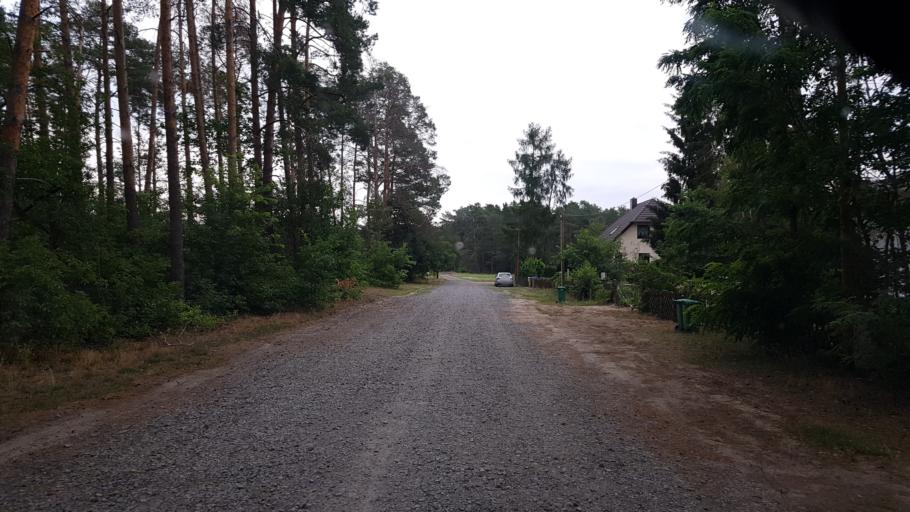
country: DE
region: Brandenburg
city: Gross Koris
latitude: 52.1616
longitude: 13.6995
